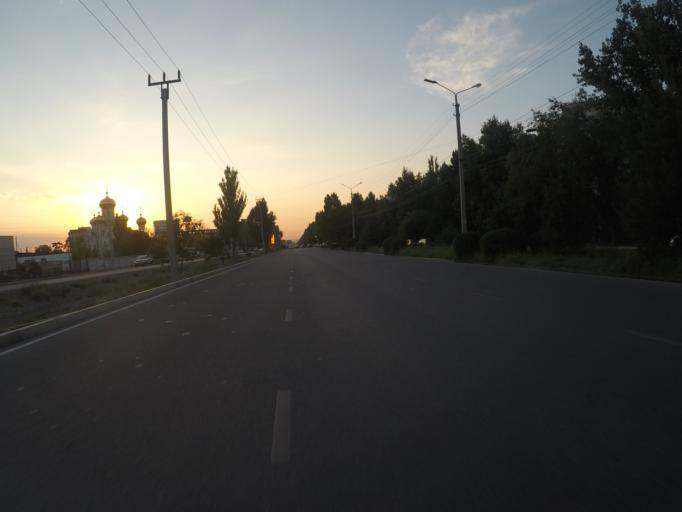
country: KG
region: Chuy
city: Bishkek
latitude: 42.8122
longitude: 74.6329
